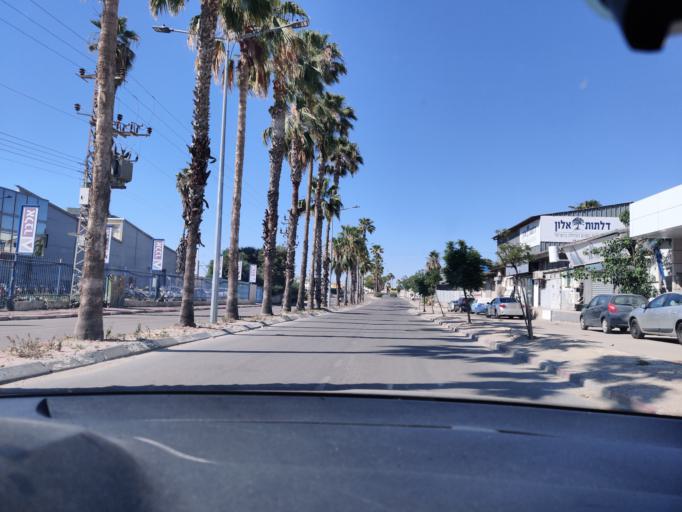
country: IL
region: Southern District
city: Qiryat Gat
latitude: 31.6000
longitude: 34.7793
